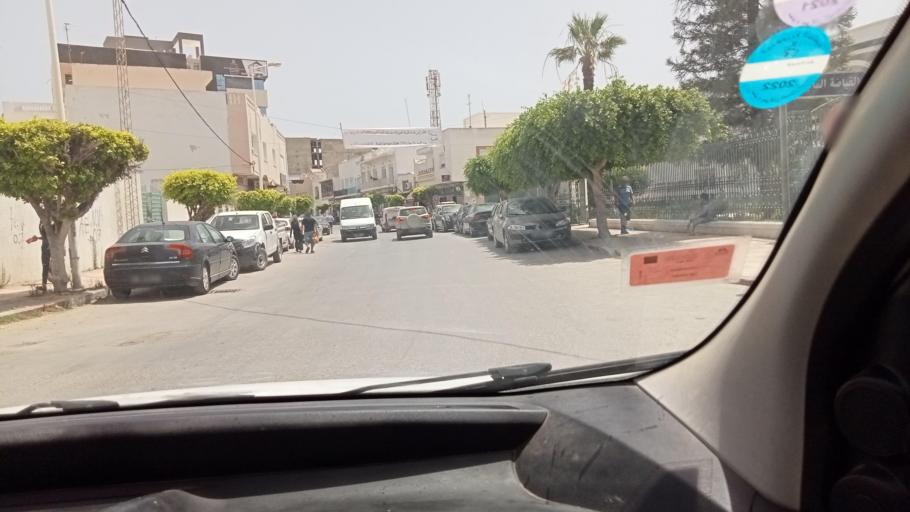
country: TN
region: Nabul
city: Qulaybiyah
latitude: 36.8465
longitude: 11.0889
